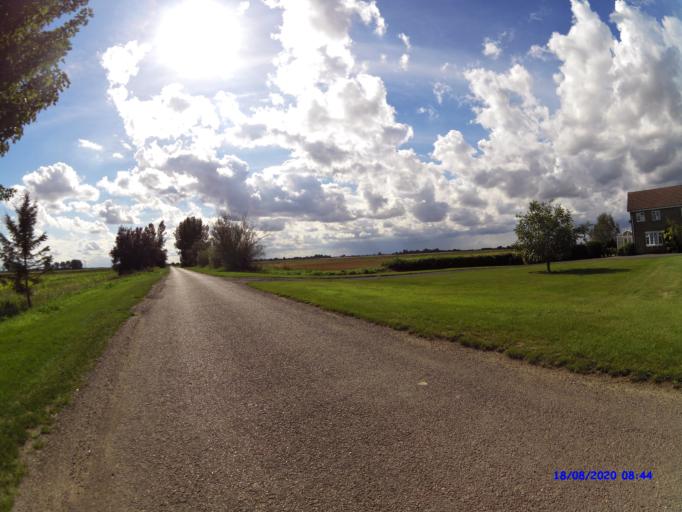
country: GB
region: England
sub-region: Cambridgeshire
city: Ramsey
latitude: 52.4905
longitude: -0.0885
